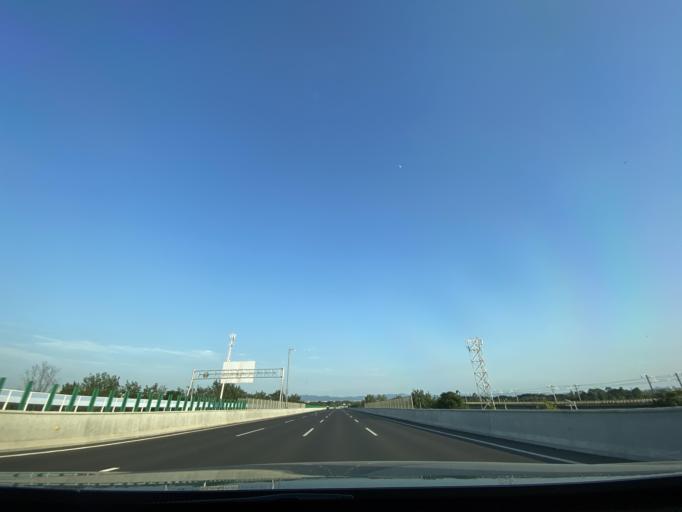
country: CN
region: Sichuan
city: Chengdu
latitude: 30.5900
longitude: 104.1243
